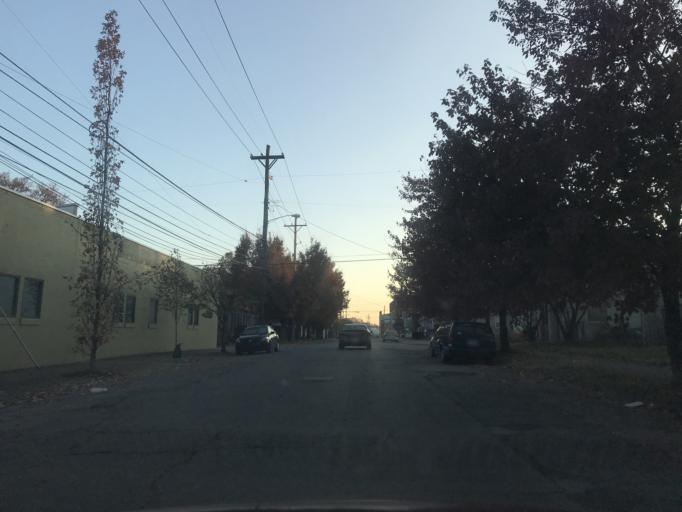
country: US
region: Kentucky
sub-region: Jefferson County
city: Louisville
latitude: 38.2497
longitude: -85.7346
